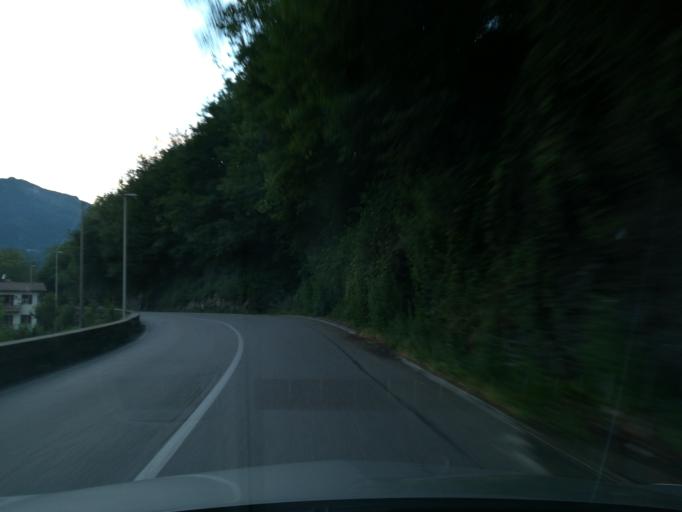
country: IT
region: Lombardy
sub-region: Provincia di Bergamo
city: Selino Basso
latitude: 45.8168
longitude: 9.5263
